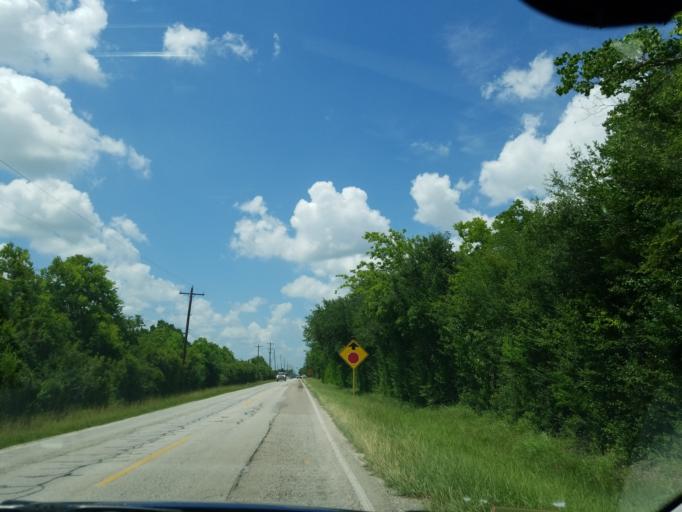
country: US
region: Texas
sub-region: Harris County
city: Katy
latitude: 29.8721
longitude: -95.8072
